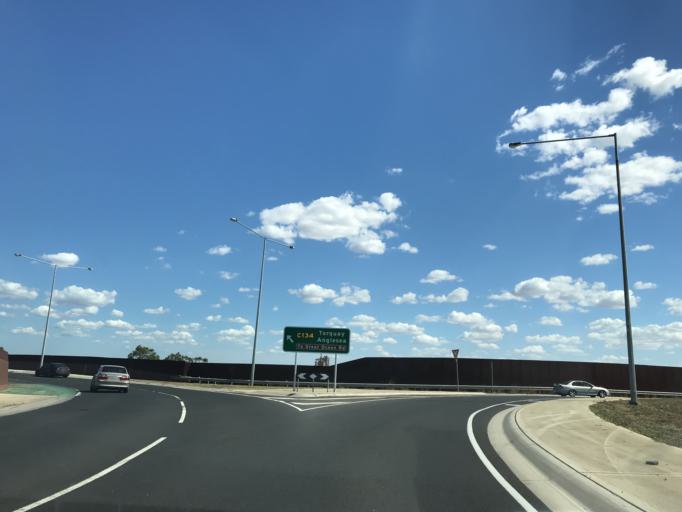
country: AU
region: Victoria
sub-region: Greater Geelong
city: Wandana Heights
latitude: -38.2190
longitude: 144.2879
